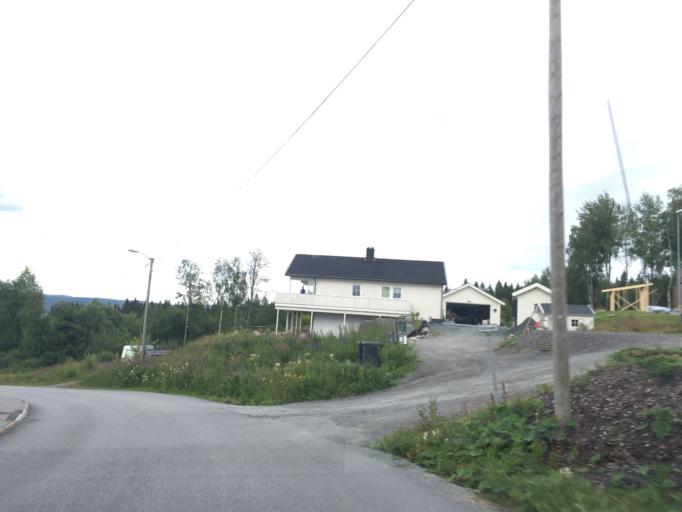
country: NO
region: Hedmark
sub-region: Kongsvinger
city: Kongsvinger
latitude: 60.1800
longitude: 11.9922
